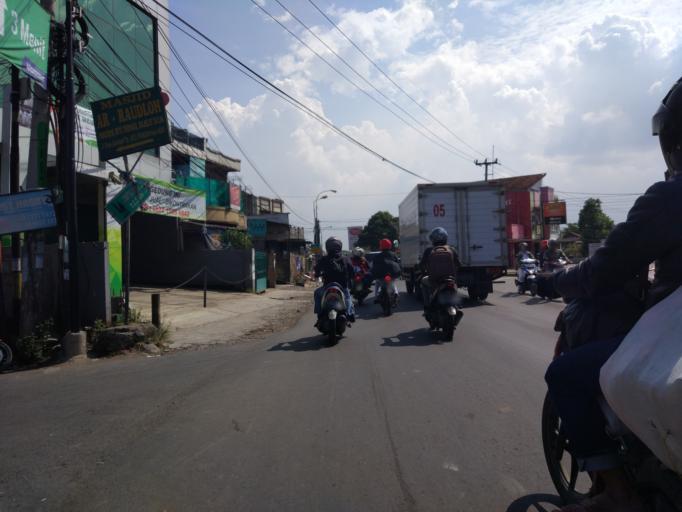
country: ID
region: West Java
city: Cileunyi
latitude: -6.9402
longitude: 107.7503
